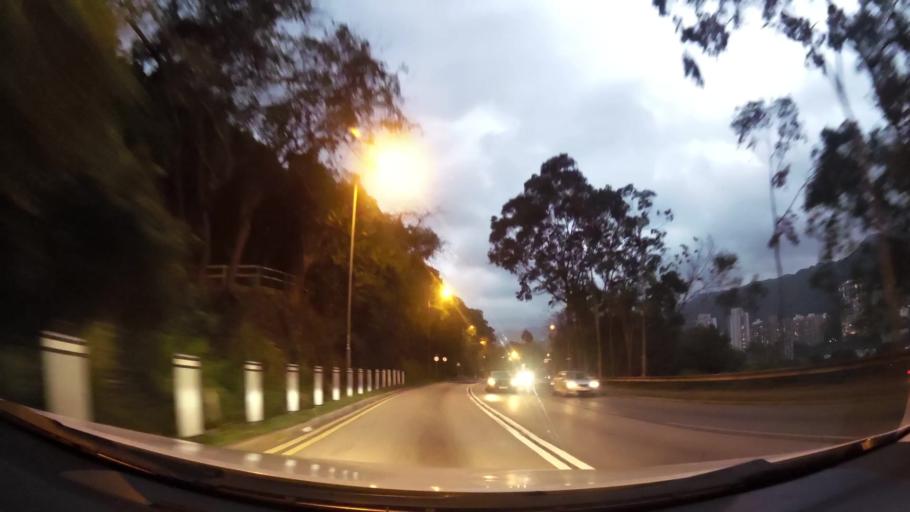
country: HK
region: Wong Tai Sin
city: Wong Tai Sin
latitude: 22.3661
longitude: 114.1674
